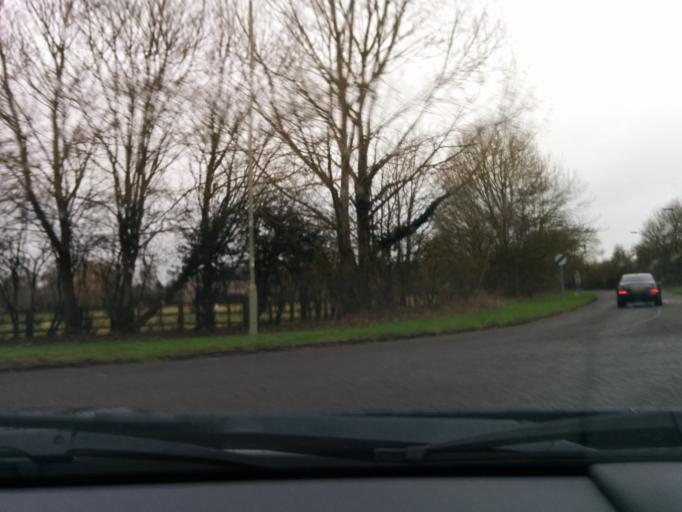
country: GB
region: England
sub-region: Oxfordshire
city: Eynsham
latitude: 51.7777
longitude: -1.3667
